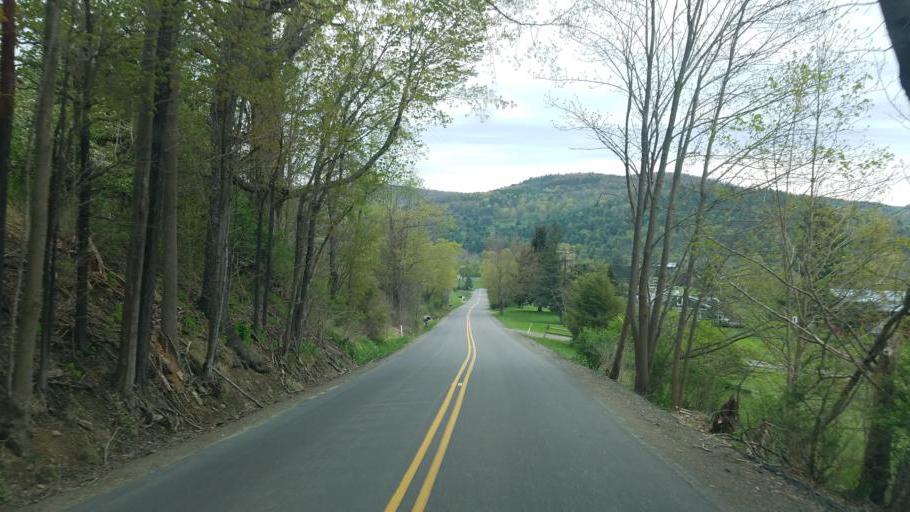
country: US
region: Pennsylvania
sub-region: Tioga County
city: Westfield
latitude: 41.9994
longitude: -77.4892
